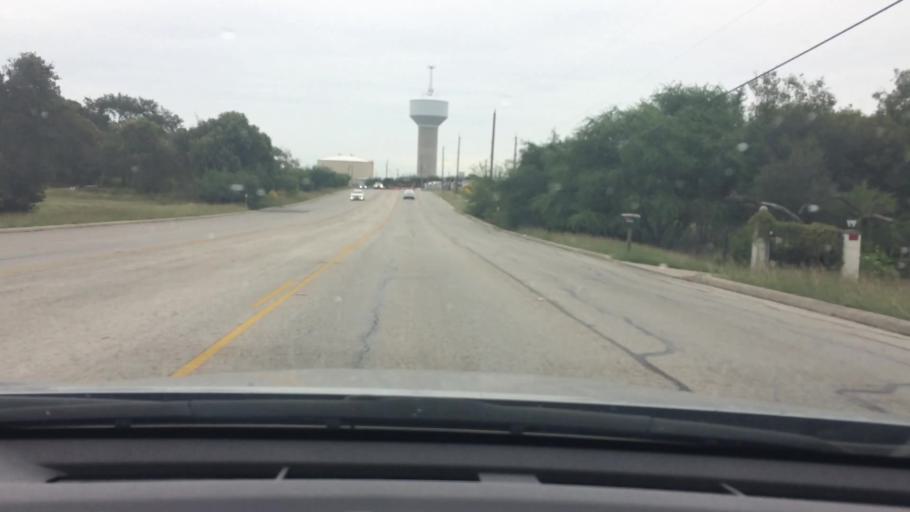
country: US
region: Texas
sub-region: Bexar County
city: Windcrest
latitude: 29.5336
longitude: -98.3574
